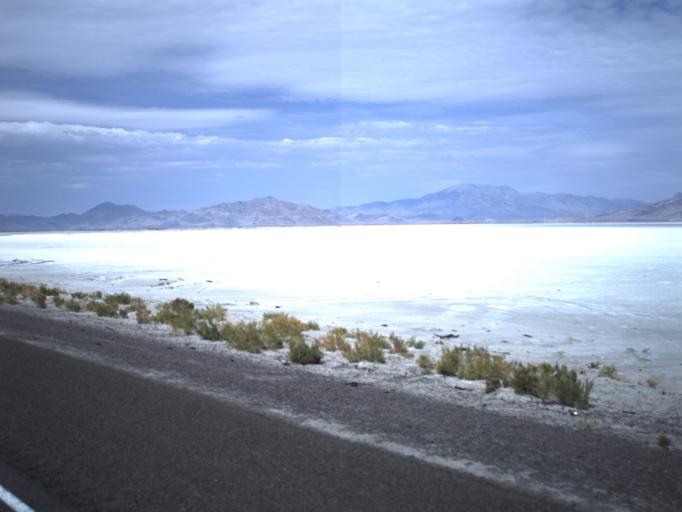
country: US
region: Utah
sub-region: Tooele County
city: Wendover
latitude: 40.7367
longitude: -113.7209
